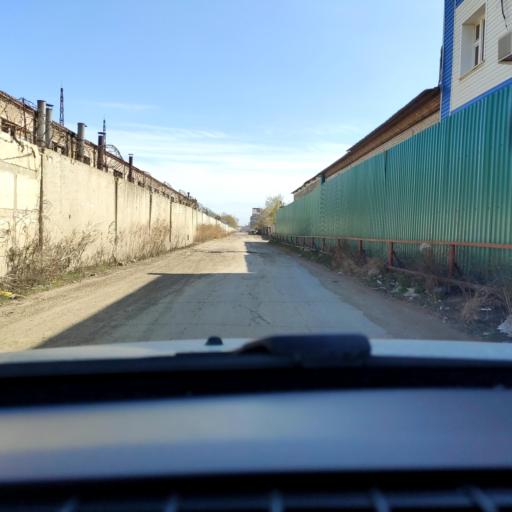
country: RU
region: Samara
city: Samara
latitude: 53.2001
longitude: 50.2711
